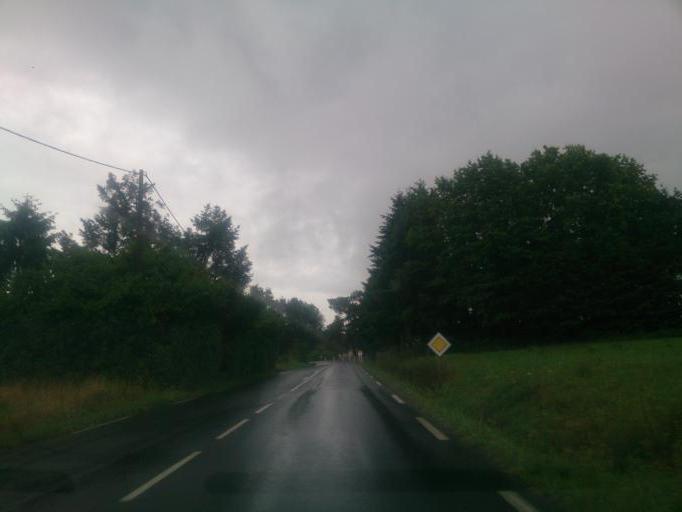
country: FR
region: Limousin
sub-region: Departement de la Correze
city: Malemort-sur-Correze
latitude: 45.1913
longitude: 1.5824
